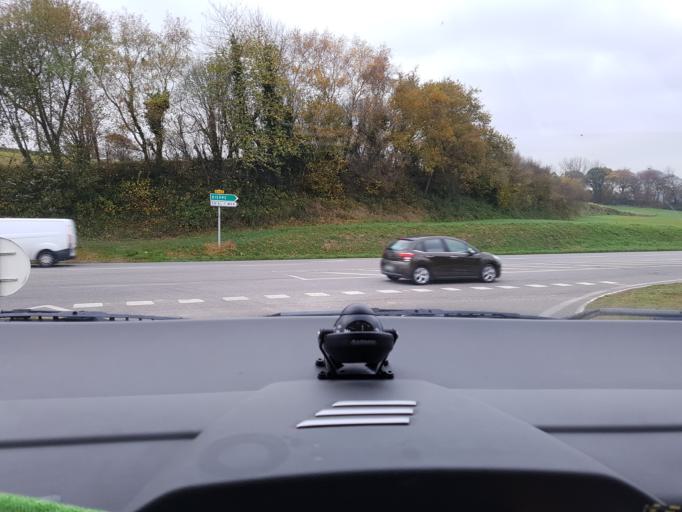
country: FR
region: Haute-Normandie
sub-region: Departement de la Seine-Maritime
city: Criel-sur-Mer
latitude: 50.0236
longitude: 1.3447
